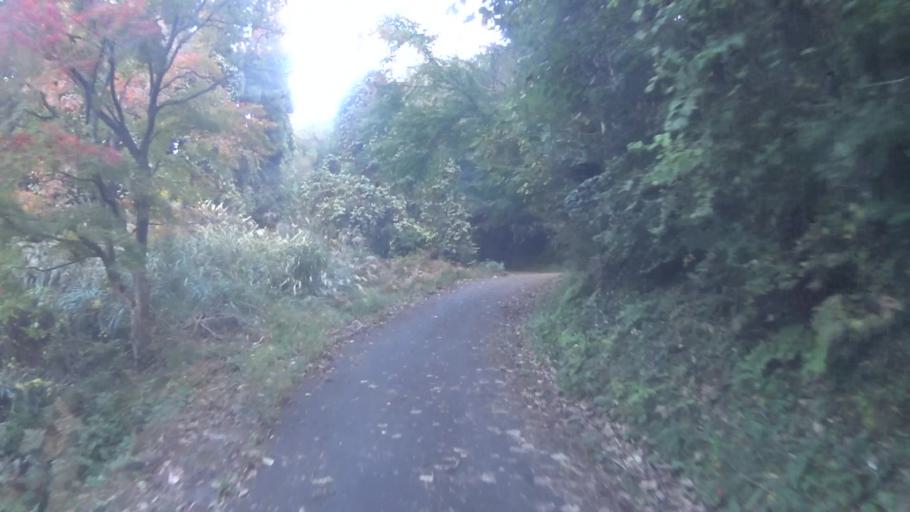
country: JP
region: Kyoto
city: Ayabe
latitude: 35.2676
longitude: 135.2468
